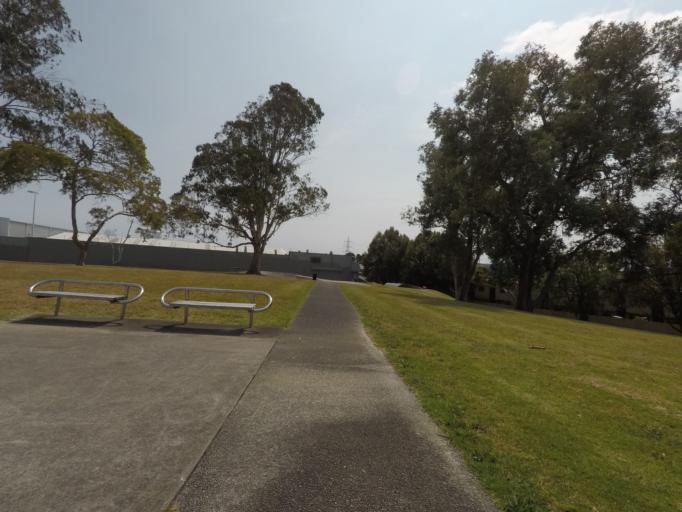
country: NZ
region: Auckland
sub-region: Auckland
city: Waitakere
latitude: -36.9149
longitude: 174.6894
